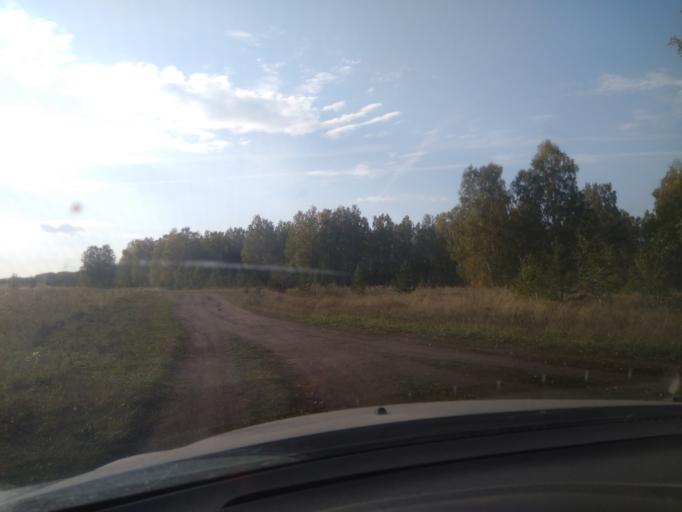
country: RU
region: Sverdlovsk
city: Pokrovskoye
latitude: 56.4298
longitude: 61.6078
